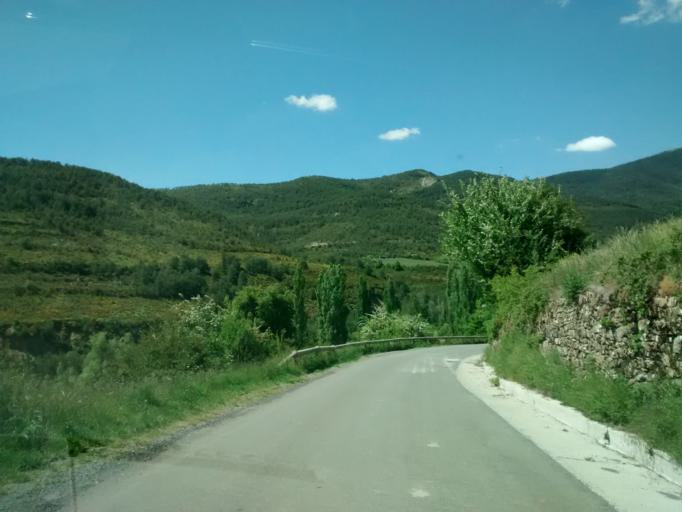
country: ES
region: Aragon
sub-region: Provincia de Huesca
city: Borau
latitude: 42.6820
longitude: -0.6215
